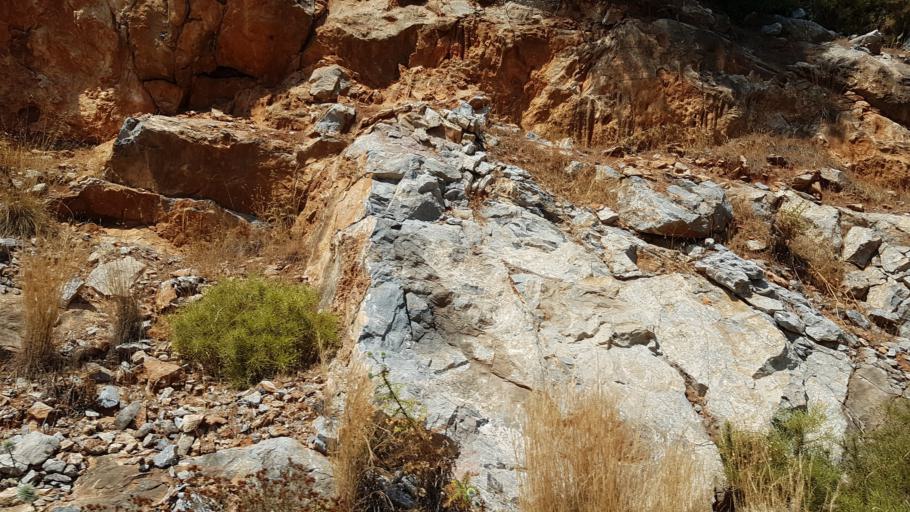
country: TR
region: Mugla
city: Karaova
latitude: 37.0462
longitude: 27.7078
